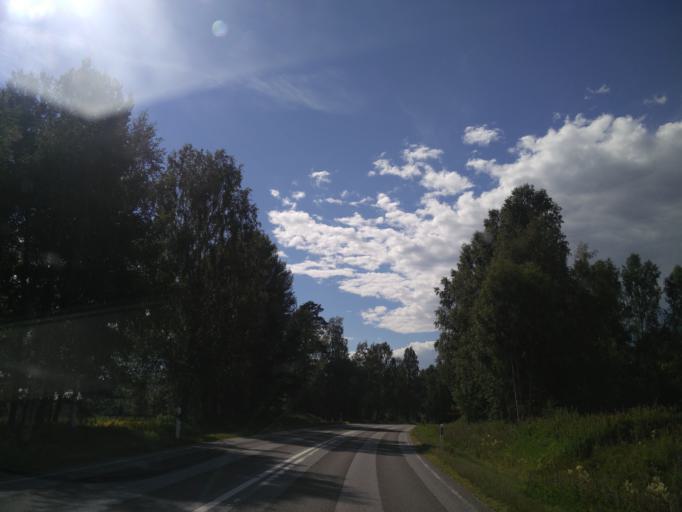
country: SE
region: OErebro
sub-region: Hallefors Kommun
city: Haellefors
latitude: 59.7387
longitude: 14.4766
